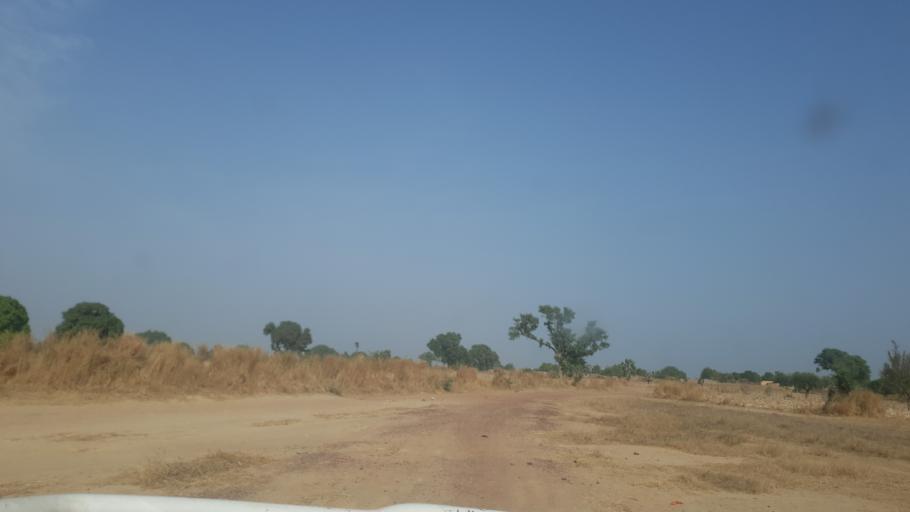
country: ML
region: Segou
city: Baroueli
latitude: 13.3533
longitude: -6.9377
